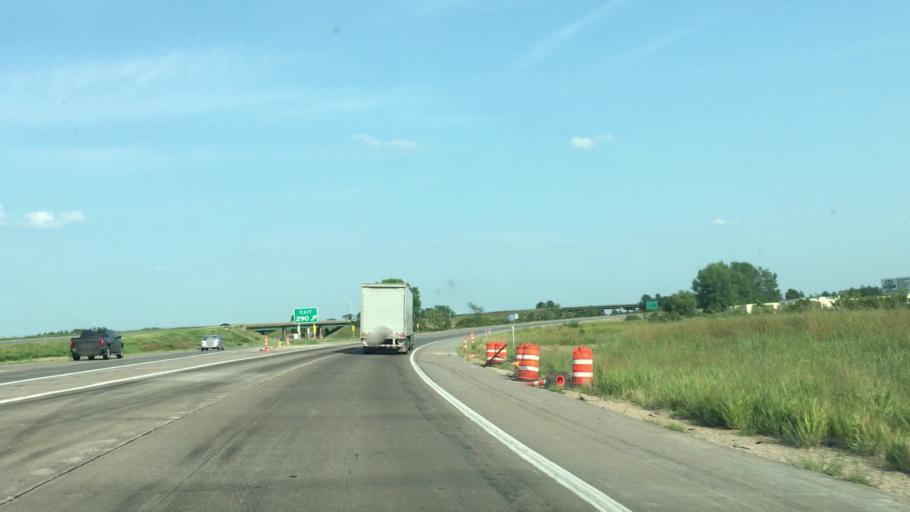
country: US
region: Iowa
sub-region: Scott County
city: Walcott
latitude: 41.6034
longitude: -90.6824
